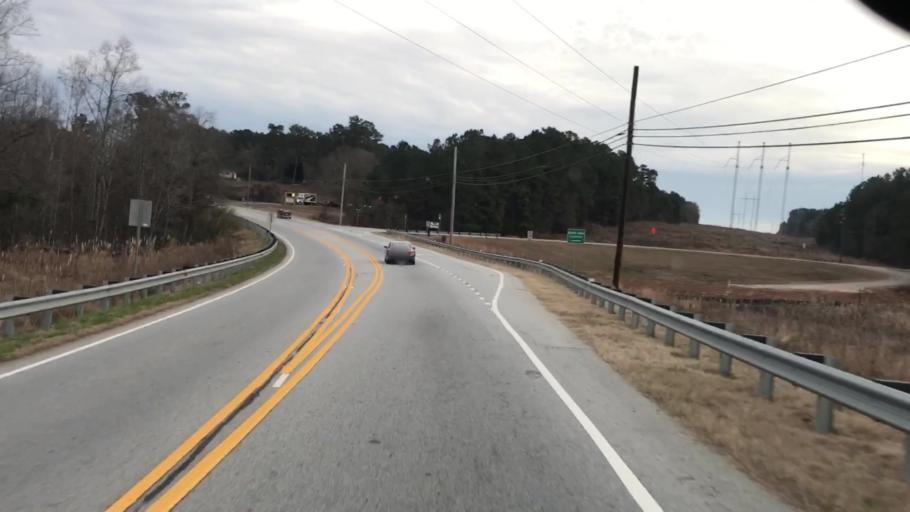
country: US
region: Georgia
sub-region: Barrow County
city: Winder
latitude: 34.0063
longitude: -83.7554
